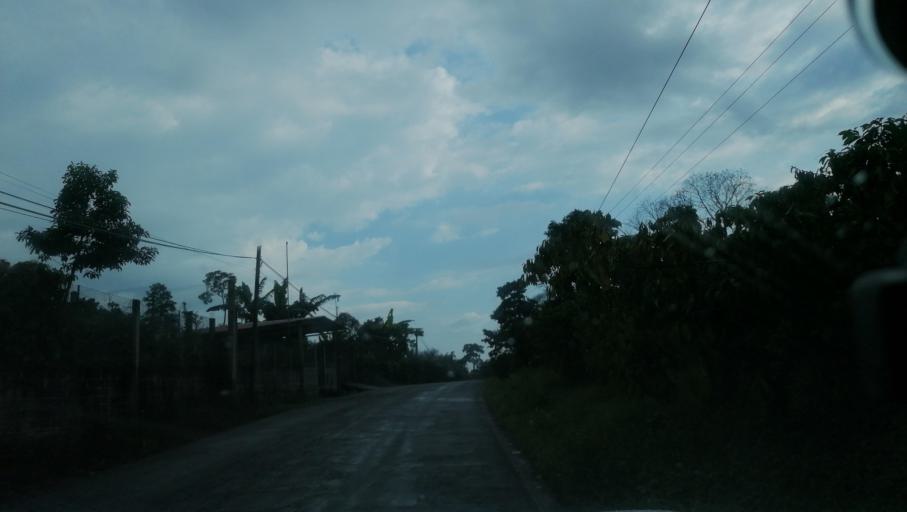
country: MX
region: Chiapas
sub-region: Cacahoatan
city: Benito Juarez
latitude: 15.0481
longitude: -92.1866
